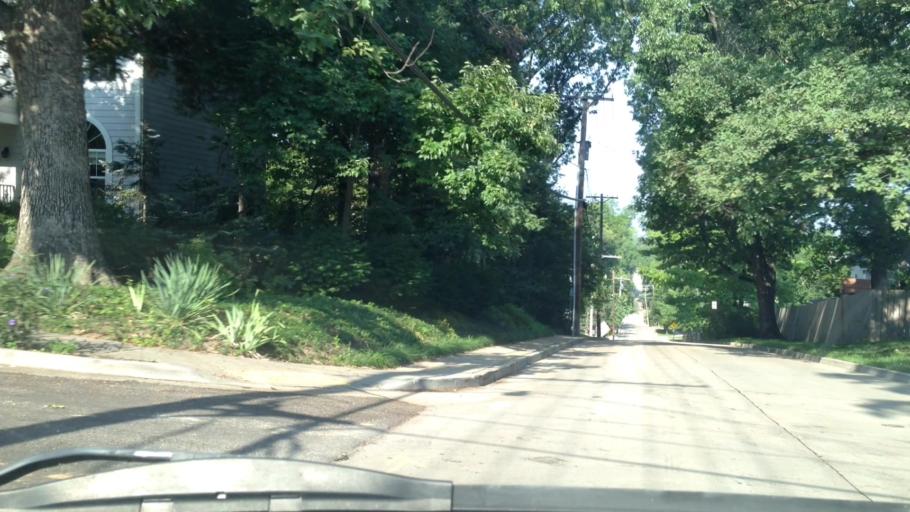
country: US
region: Missouri
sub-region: Saint Louis County
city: Kirkwood
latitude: 38.5755
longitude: -90.4277
